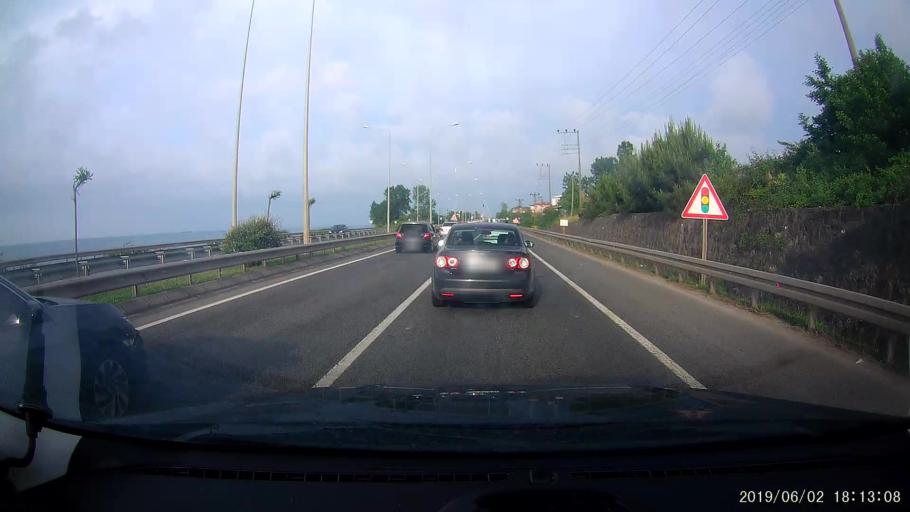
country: TR
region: Ordu
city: Unieh
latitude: 41.1065
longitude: 37.3673
